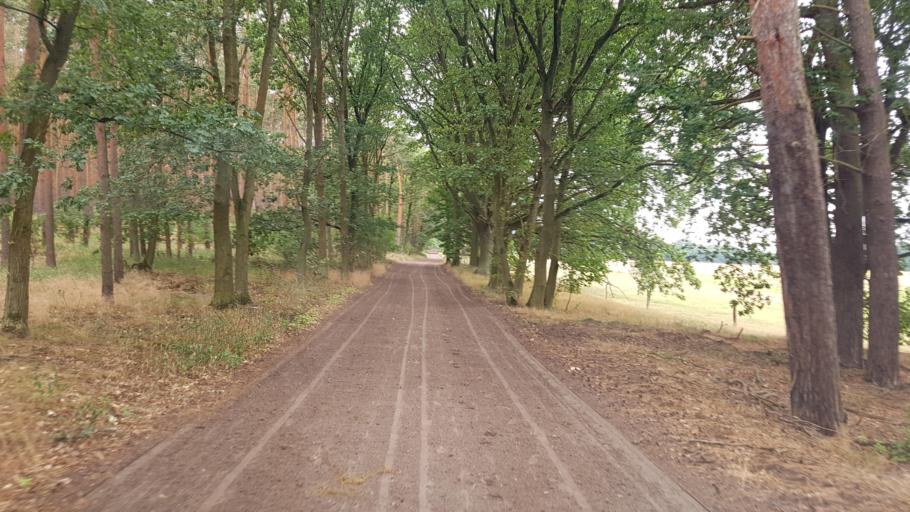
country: DE
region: Brandenburg
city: Trebbin
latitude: 52.2533
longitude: 13.1708
